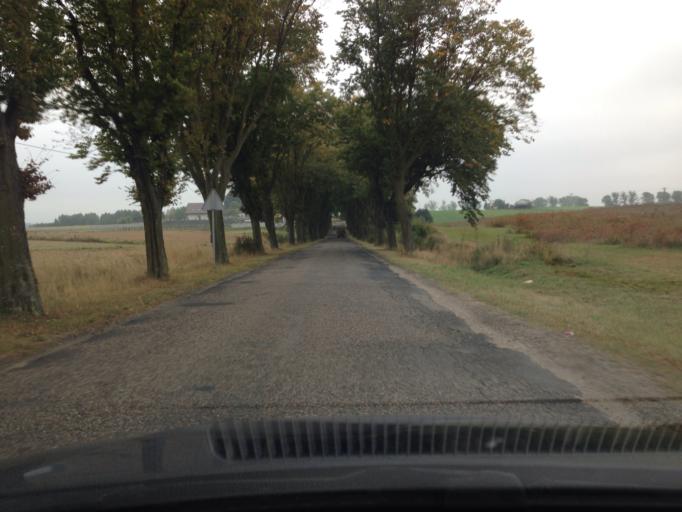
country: PL
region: Kujawsko-Pomorskie
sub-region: Powiat brodnicki
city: Gorzno
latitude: 53.2124
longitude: 19.6353
